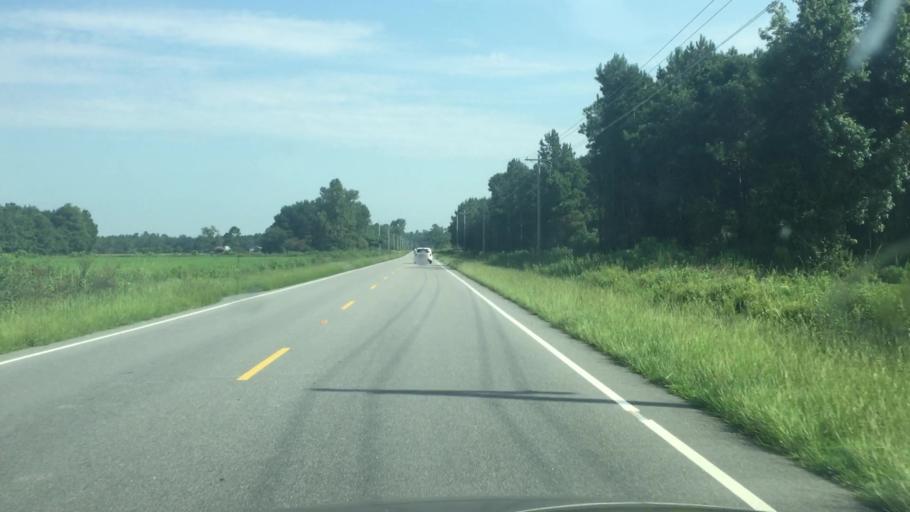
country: US
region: North Carolina
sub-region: Columbus County
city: Tabor City
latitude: 34.2223
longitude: -78.8241
